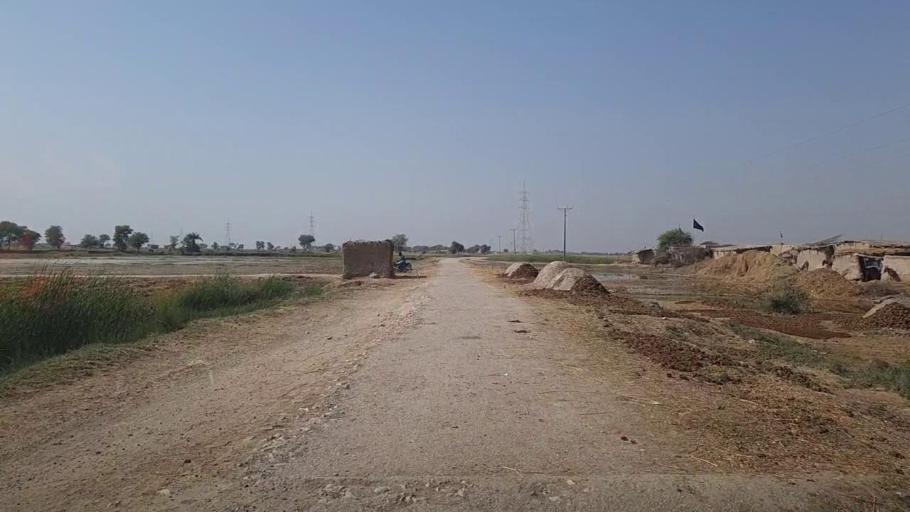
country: PK
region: Sindh
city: Kandhkot
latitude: 28.4092
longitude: 69.2475
